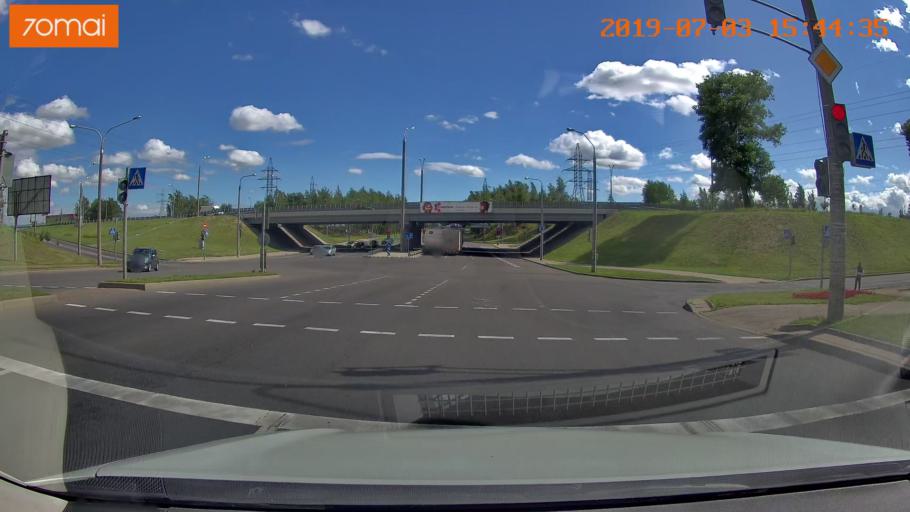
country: BY
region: Minsk
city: Syenitsa
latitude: 53.8340
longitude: 27.5747
